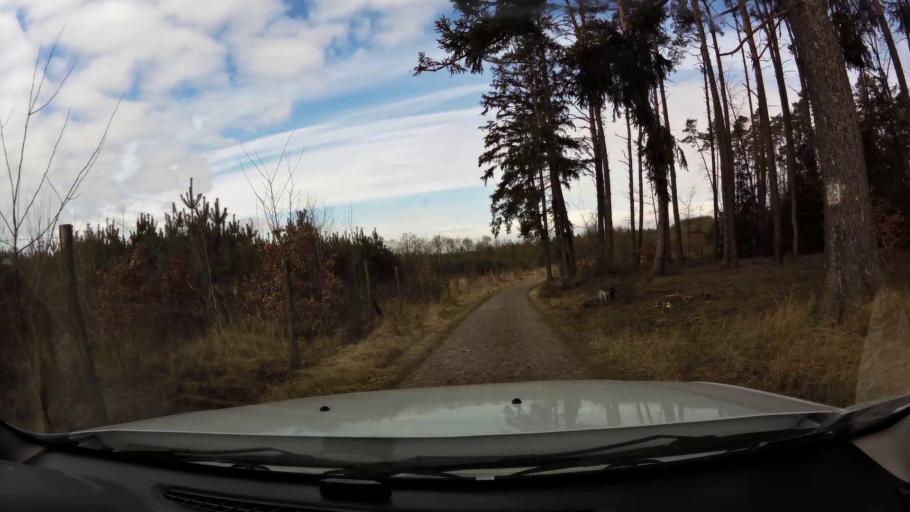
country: PL
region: West Pomeranian Voivodeship
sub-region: Powiat mysliborski
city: Debno
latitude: 52.8435
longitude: 14.6862
